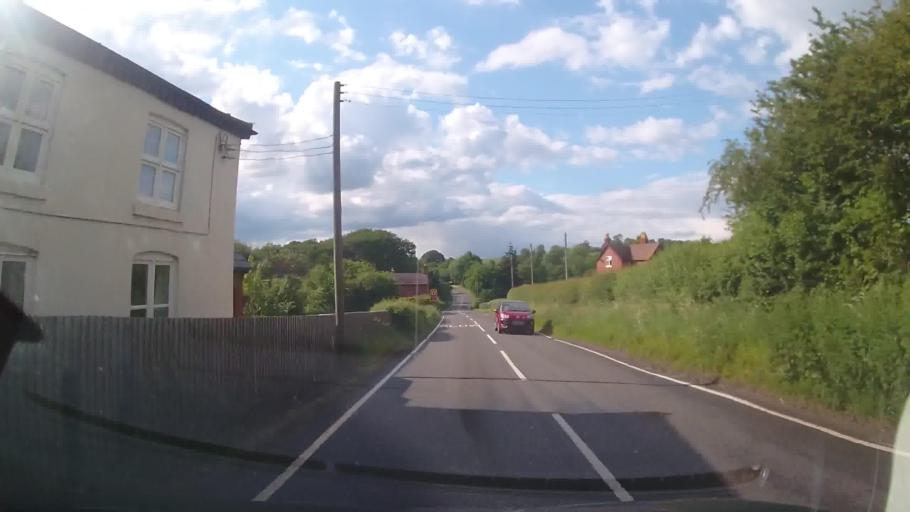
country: GB
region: England
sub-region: Shropshire
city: Harley
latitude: 52.6533
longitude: -2.6096
